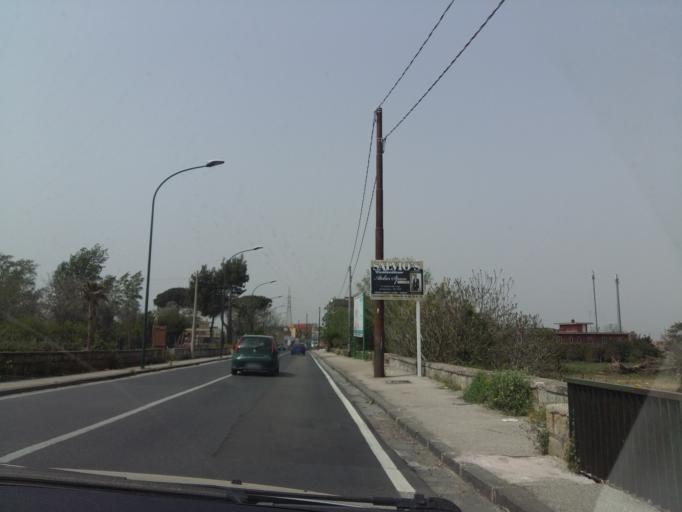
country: IT
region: Campania
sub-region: Provincia di Napoli
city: Mugnano di Napoli
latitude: 40.8966
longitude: 14.2130
